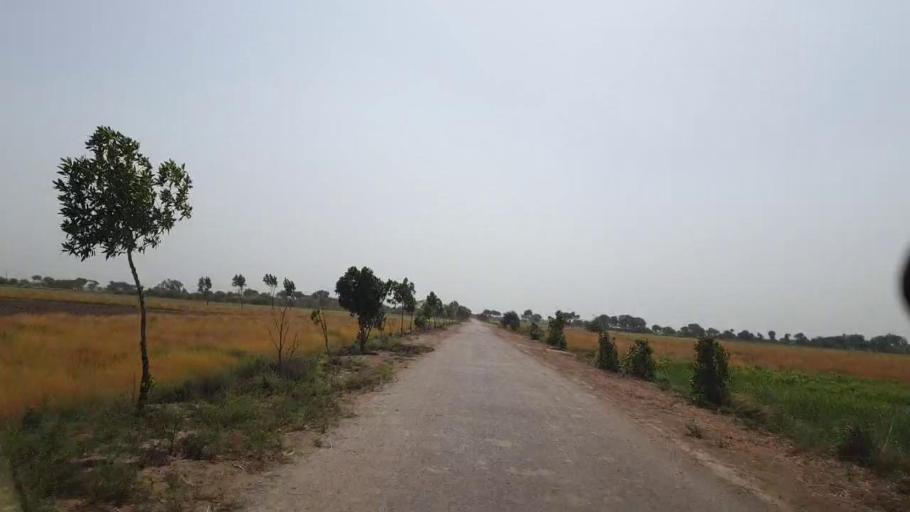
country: PK
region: Sindh
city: Matli
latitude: 25.0452
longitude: 68.6850
